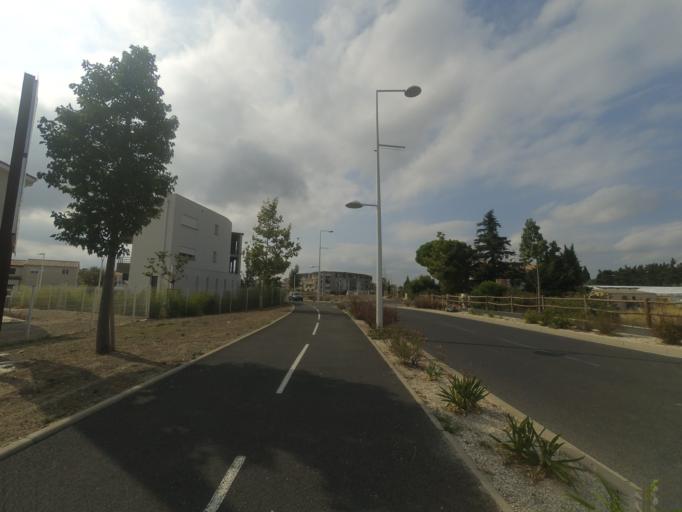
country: FR
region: Languedoc-Roussillon
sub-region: Departement des Pyrenees-Orientales
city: Villeneuve-la-Riviere
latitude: 42.6793
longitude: 2.8092
